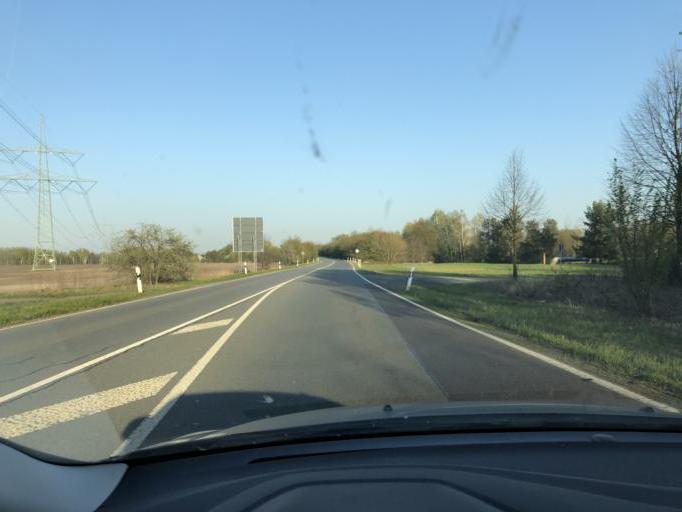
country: DE
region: Brandenburg
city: Ruhland
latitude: 51.4651
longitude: 13.8699
